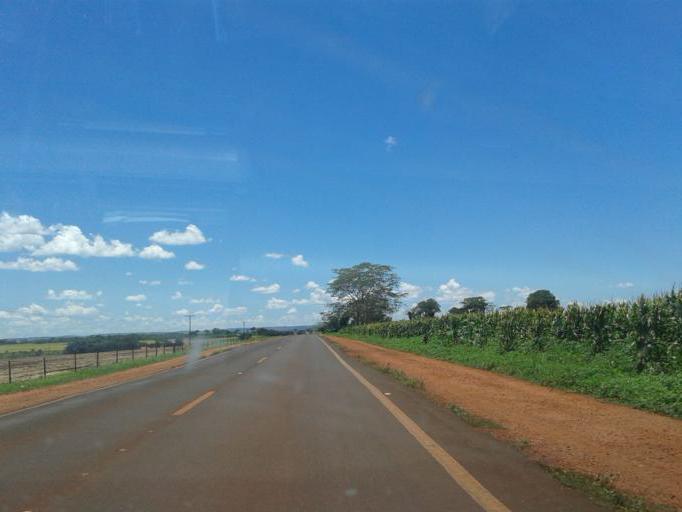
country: BR
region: Minas Gerais
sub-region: Capinopolis
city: Capinopolis
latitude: -18.6098
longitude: -49.5274
